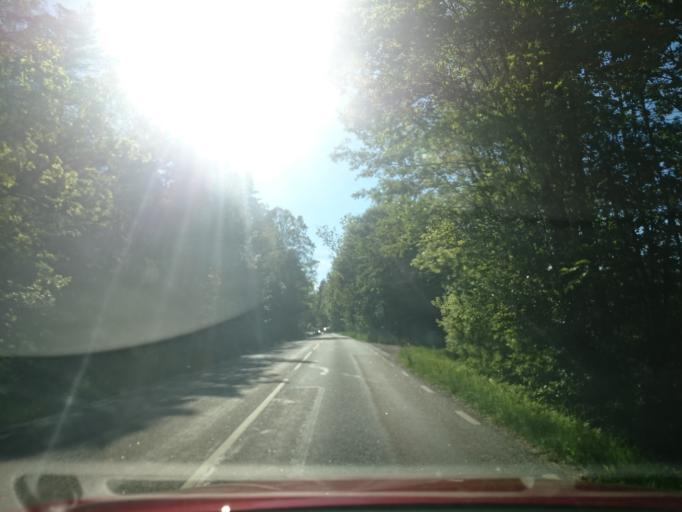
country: SE
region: Vaestra Goetaland
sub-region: Lysekils Kommun
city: Lysekil
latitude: 58.2567
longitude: 11.5259
